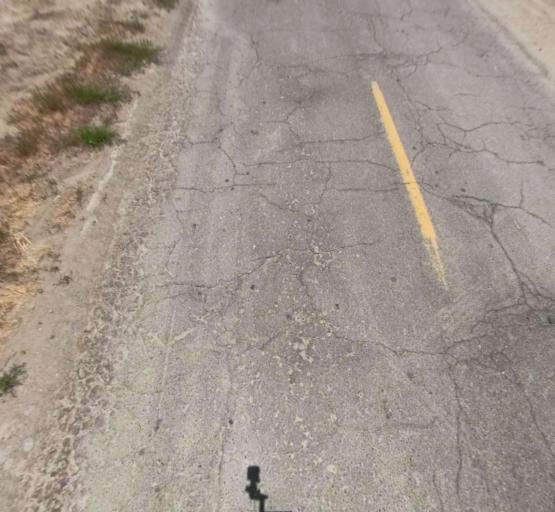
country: US
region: California
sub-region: Fresno County
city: Biola
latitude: 36.8453
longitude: -120.0921
